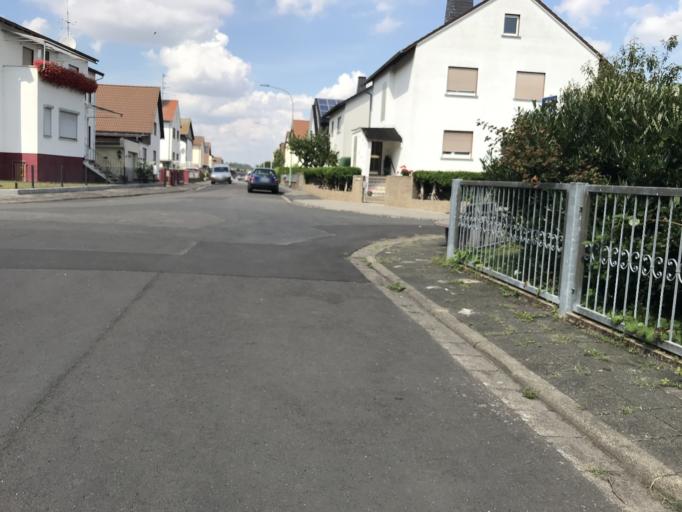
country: DE
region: Hesse
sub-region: Regierungsbezirk Darmstadt
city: Wolfersheim
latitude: 50.3973
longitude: 8.8228
